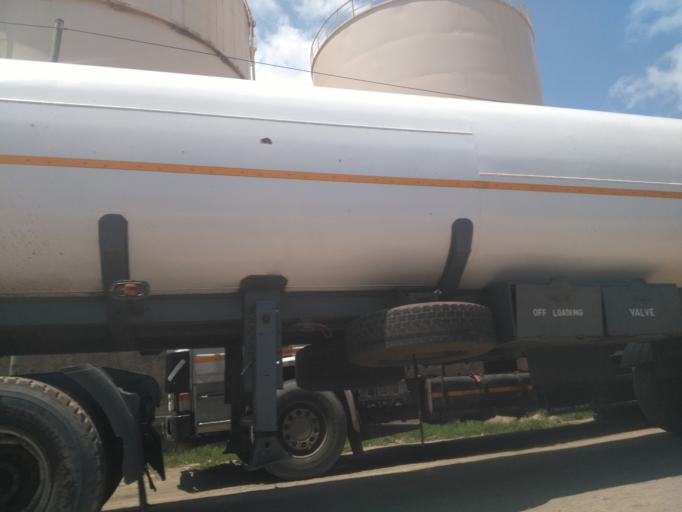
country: TZ
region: Dar es Salaam
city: Dar es Salaam
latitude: -6.8402
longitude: 39.2916
